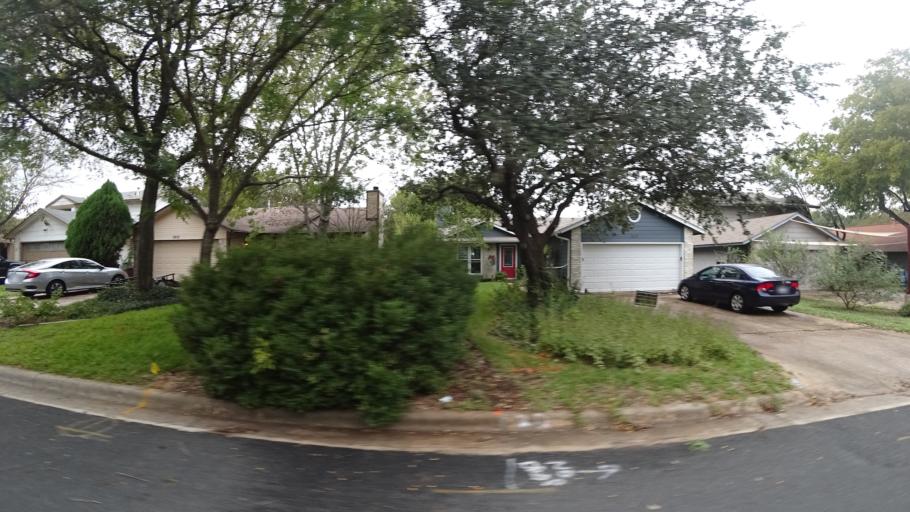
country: US
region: Texas
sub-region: Travis County
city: Shady Hollow
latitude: 30.2025
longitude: -97.8441
